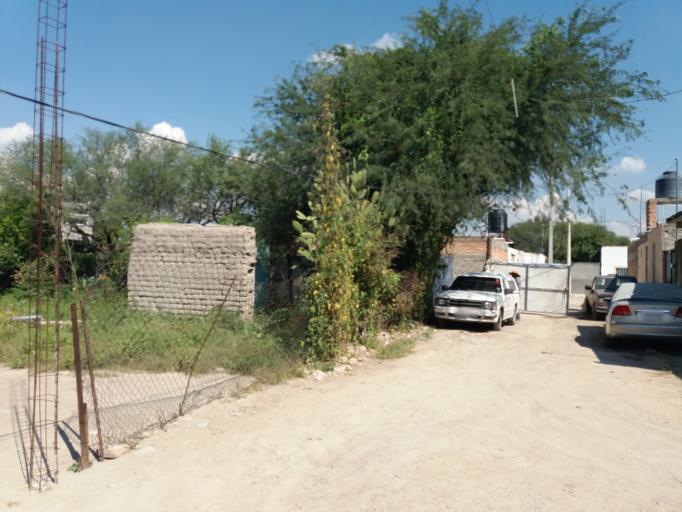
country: MX
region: Aguascalientes
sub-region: Aguascalientes
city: Penuelas (El Cienegal)
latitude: 21.7567
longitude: -102.3028
